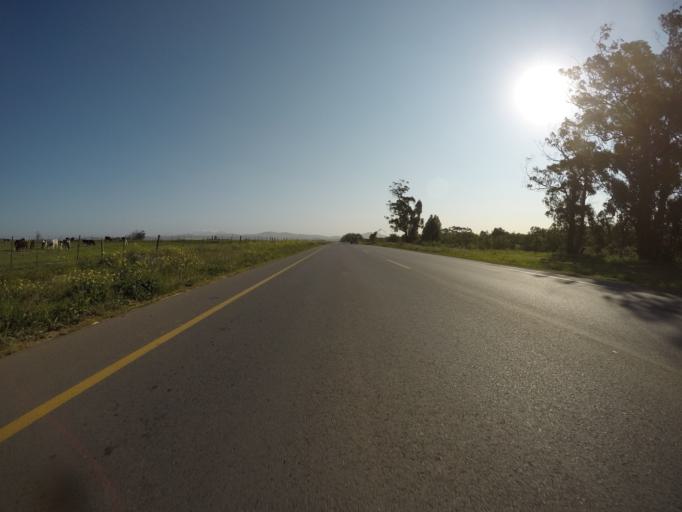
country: ZA
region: Western Cape
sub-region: City of Cape Town
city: Kraaifontein
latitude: -33.7757
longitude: 18.7408
